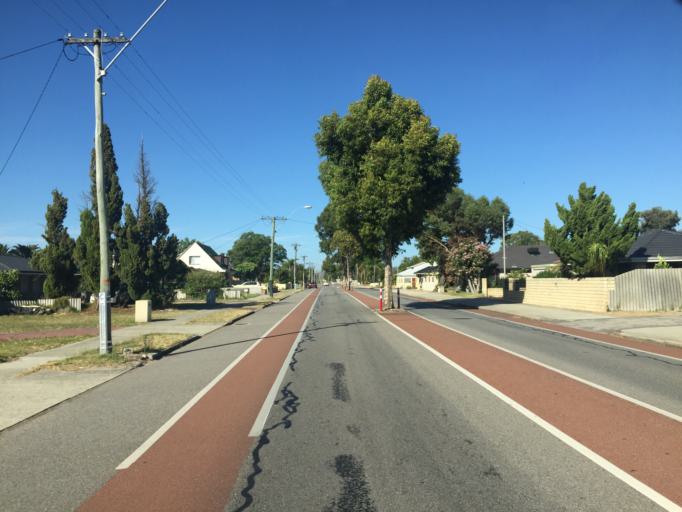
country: AU
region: Western Australia
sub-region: Canning
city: East Cannington
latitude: -32.0173
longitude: 115.9609
